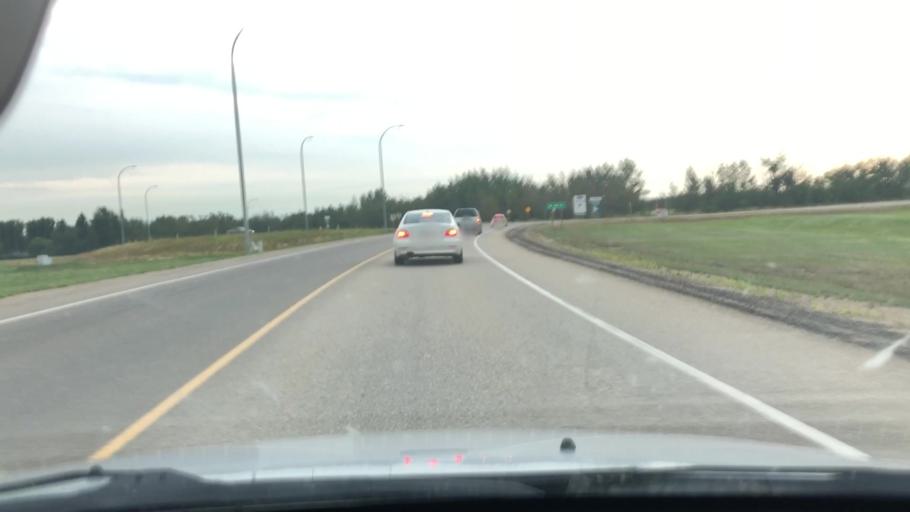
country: CA
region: Alberta
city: Devon
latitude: 53.4608
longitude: -113.6379
